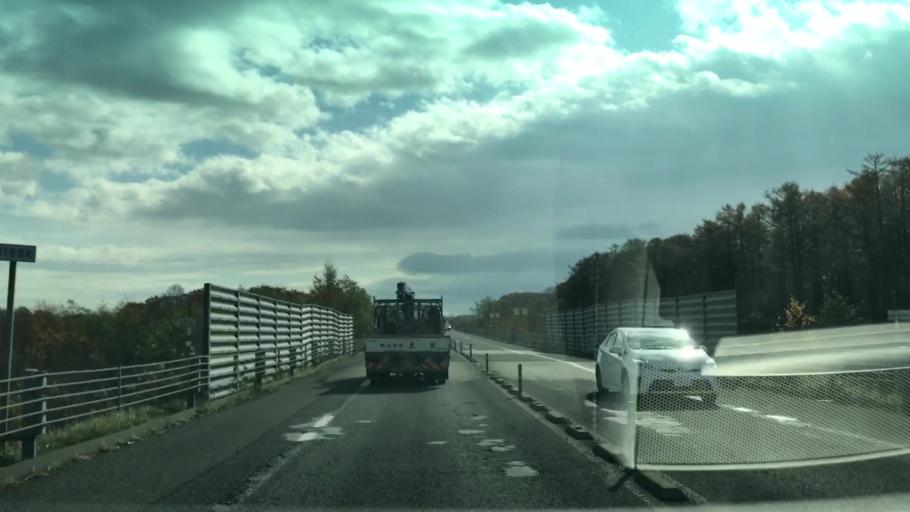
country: JP
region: Hokkaido
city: Tomakomai
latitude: 42.5694
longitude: 141.9762
